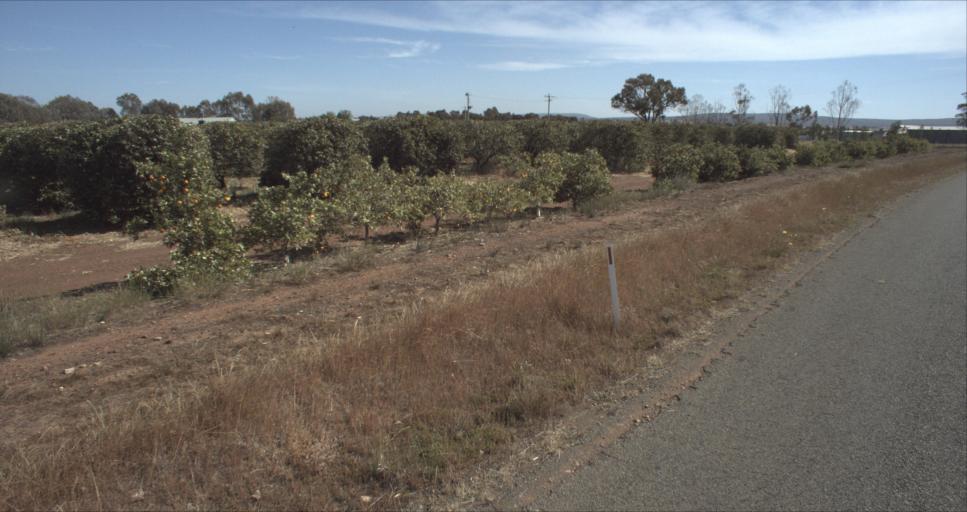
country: AU
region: New South Wales
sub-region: Leeton
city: Leeton
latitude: -34.5790
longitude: 146.4780
